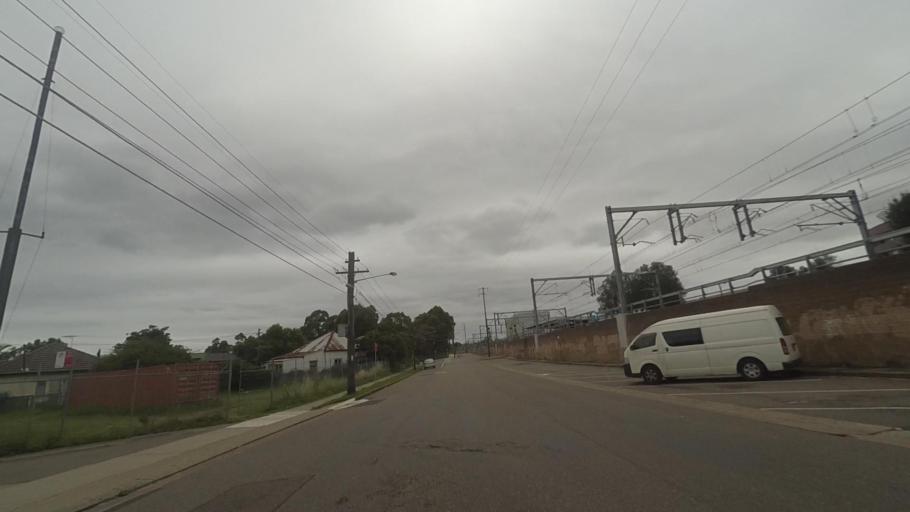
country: AU
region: New South Wales
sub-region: Auburn
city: Auburn
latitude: -33.8530
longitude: 151.0360
